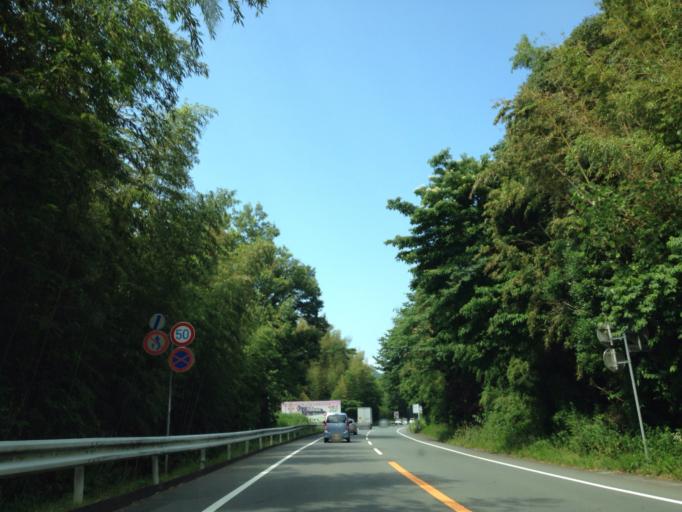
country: JP
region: Shizuoka
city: Mishima
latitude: 35.0466
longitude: 138.9210
